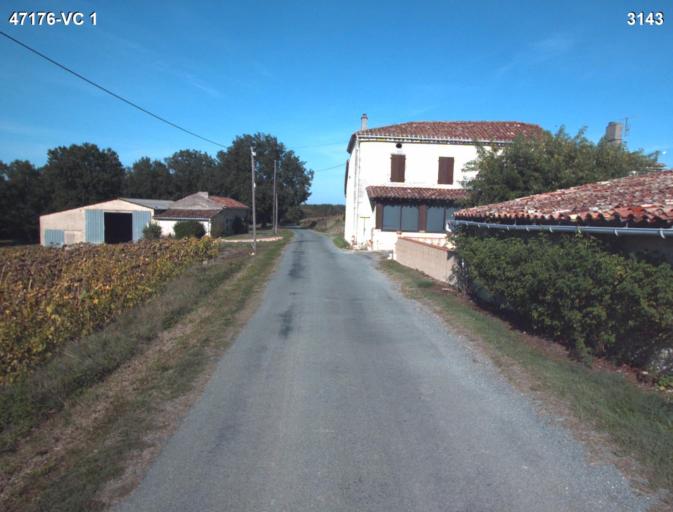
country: FR
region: Aquitaine
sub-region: Departement du Lot-et-Garonne
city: Vianne
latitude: 44.2181
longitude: 0.3038
